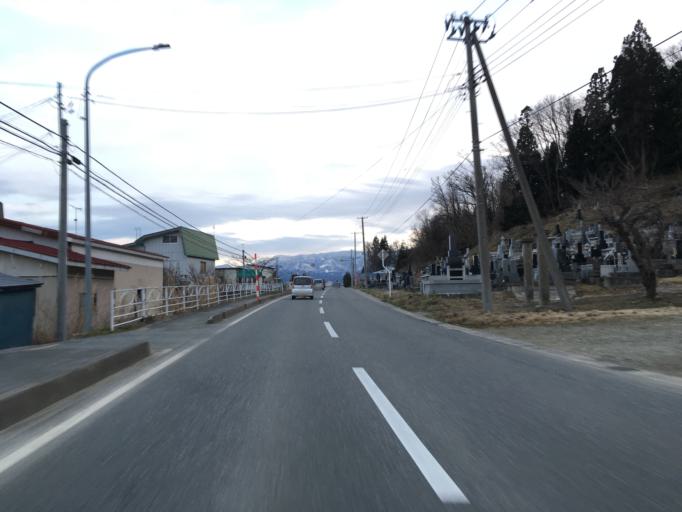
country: JP
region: Yamagata
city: Yonezawa
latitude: 37.9434
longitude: 140.0749
